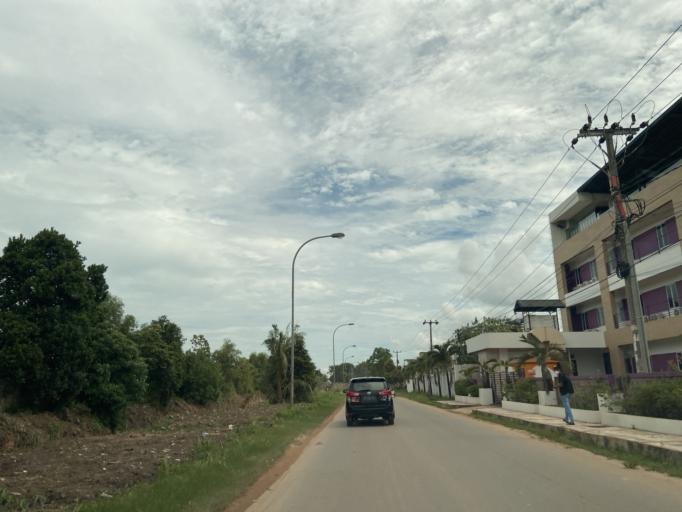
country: SG
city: Singapore
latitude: 1.0402
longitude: 103.9771
